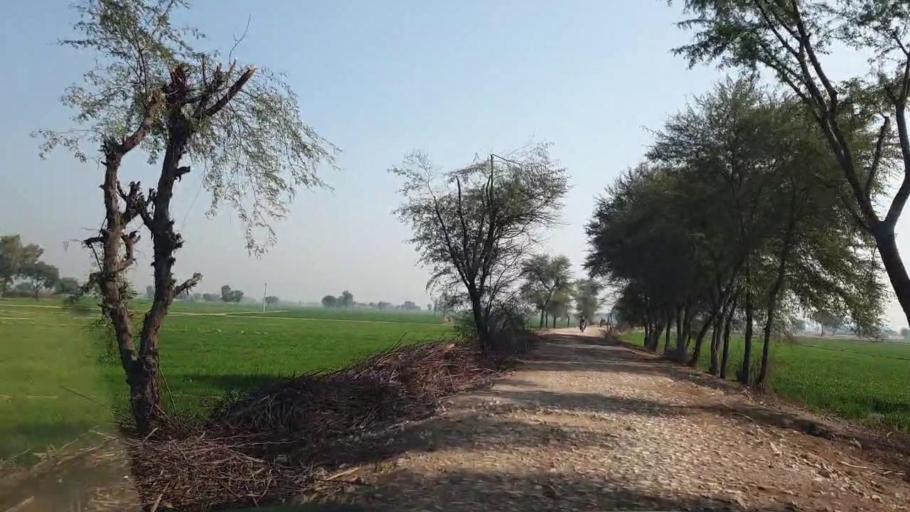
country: PK
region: Sindh
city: Ubauro
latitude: 28.1147
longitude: 69.7872
